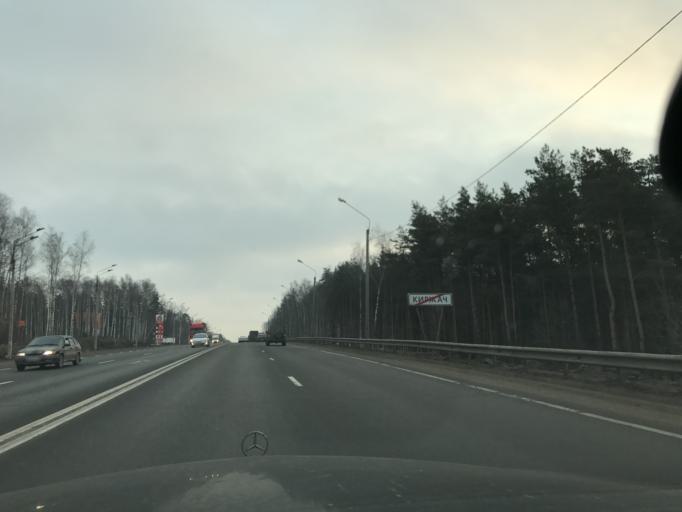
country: RU
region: Vladimir
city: Pokrov
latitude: 55.9014
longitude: 39.0782
